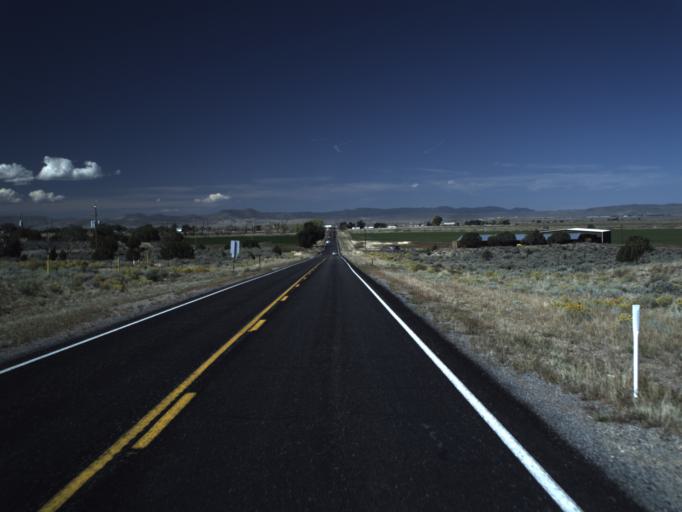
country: US
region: Utah
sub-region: Washington County
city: Enterprise
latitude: 37.6741
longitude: -113.5297
